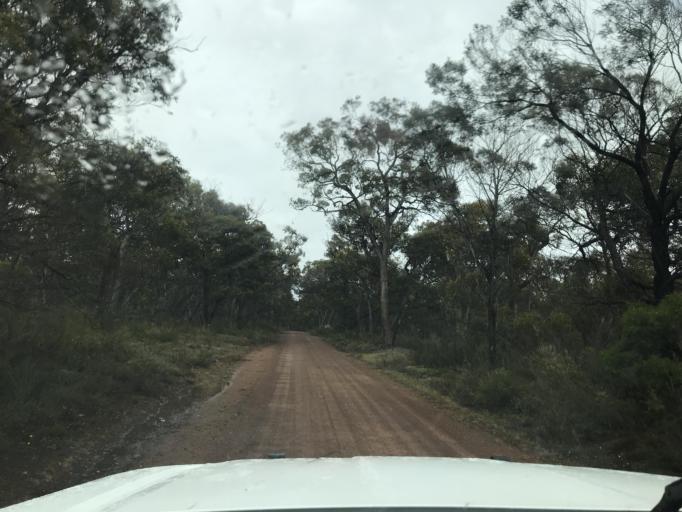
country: AU
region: South Australia
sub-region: Wattle Range
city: Penola
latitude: -37.2596
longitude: 141.3328
